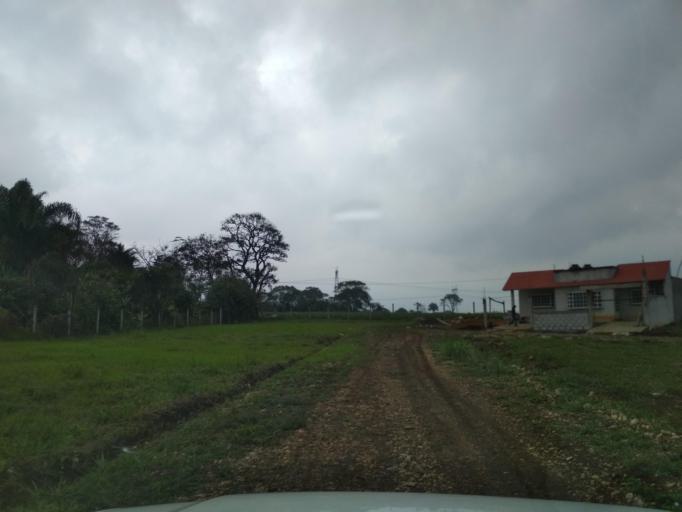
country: MX
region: Veracruz
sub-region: Cordoba
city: Veinte de Noviembre
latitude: 18.8613
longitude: -96.9648
